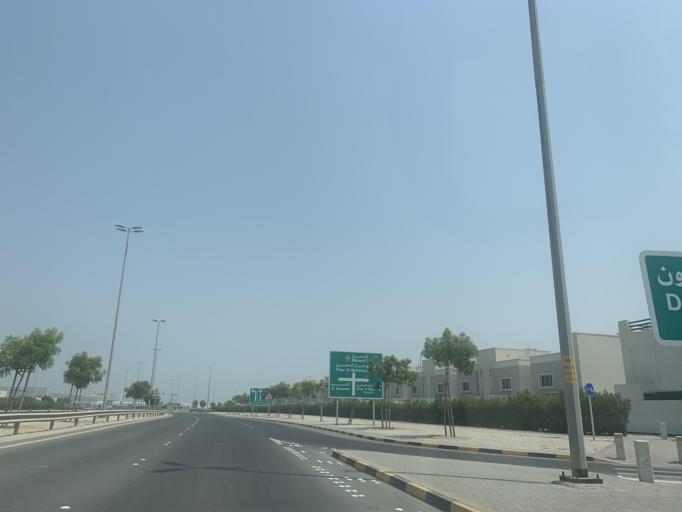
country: BH
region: Muharraq
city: Al Muharraq
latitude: 26.3116
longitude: 50.6287
